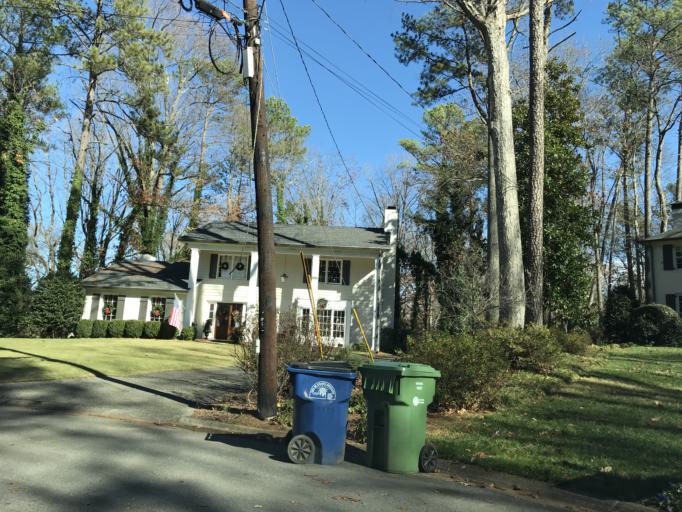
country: US
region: Georgia
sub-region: DeKalb County
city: North Atlanta
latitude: 33.8811
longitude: -84.3487
